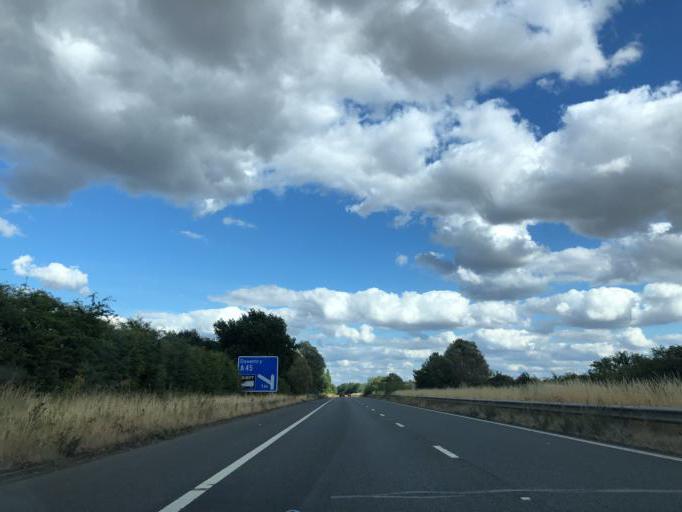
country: GB
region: England
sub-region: Warwickshire
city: Dunchurch
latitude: 52.3376
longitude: -1.3099
